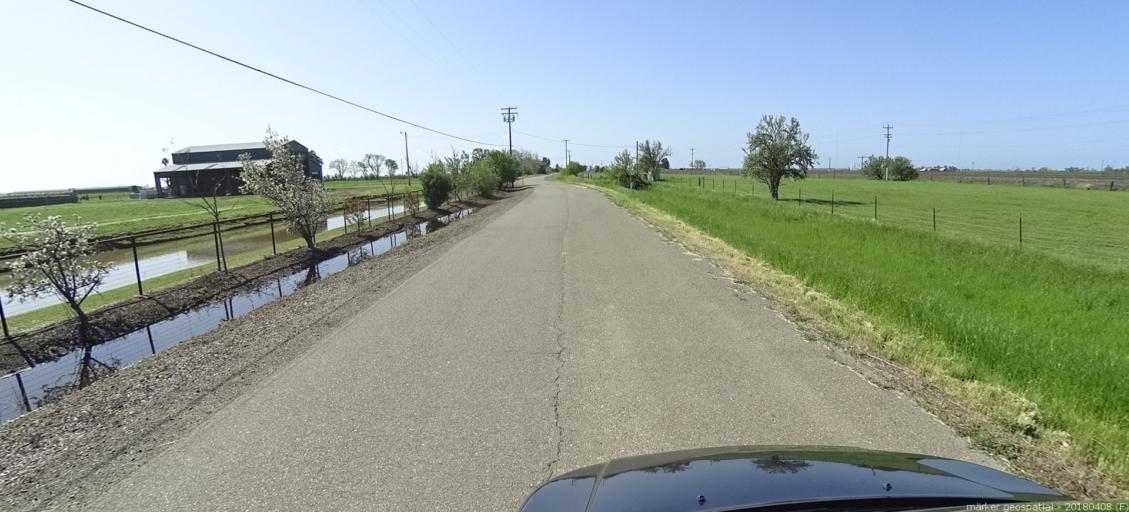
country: US
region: California
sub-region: Sacramento County
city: Laguna
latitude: 38.3368
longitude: -121.4452
